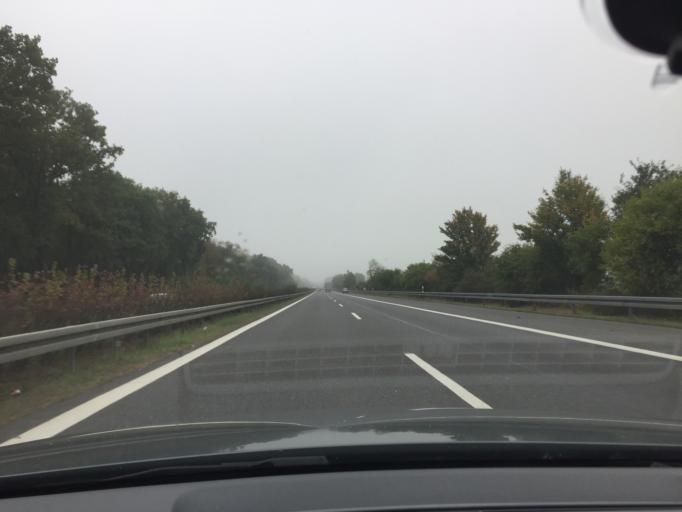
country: DE
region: Brandenburg
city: Bronkow
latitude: 51.6277
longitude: 13.9427
